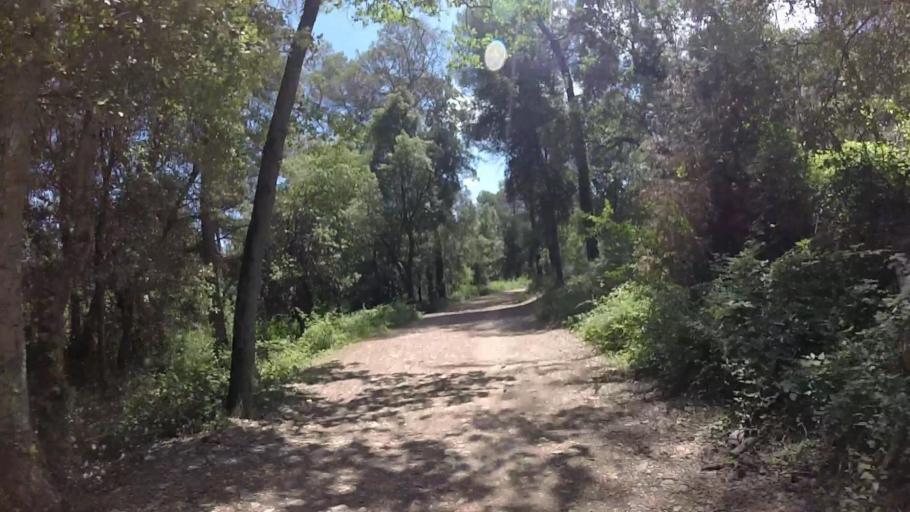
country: FR
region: Provence-Alpes-Cote d'Azur
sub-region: Departement des Alpes-Maritimes
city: Mougins
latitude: 43.5992
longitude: 7.0276
